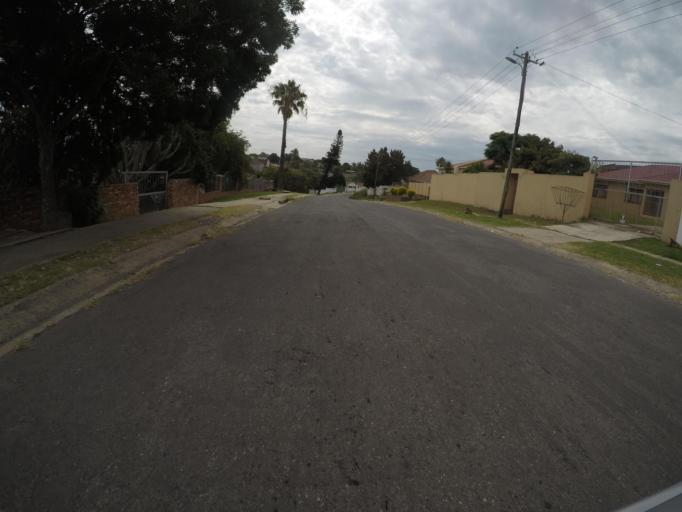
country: ZA
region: Eastern Cape
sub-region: Buffalo City Metropolitan Municipality
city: East London
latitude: -32.9972
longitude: 27.8732
